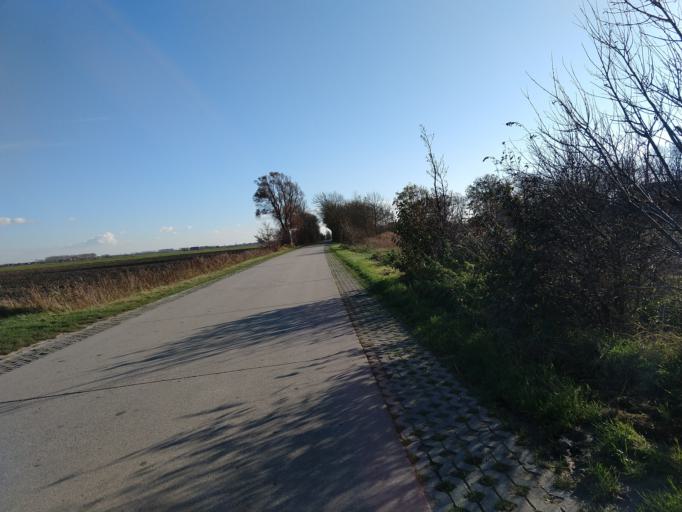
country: NL
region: Zeeland
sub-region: Gemeente Vlissingen
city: Vlissingen
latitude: 51.5264
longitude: 3.4823
